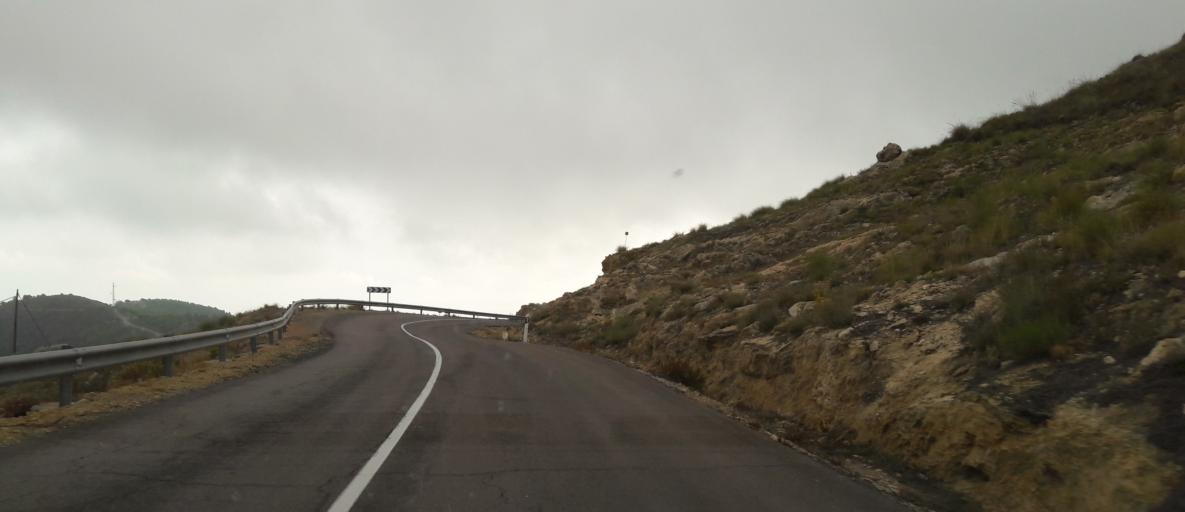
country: ES
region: Andalusia
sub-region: Provincia de Almeria
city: Enix
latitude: 36.8761
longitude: -2.6224
